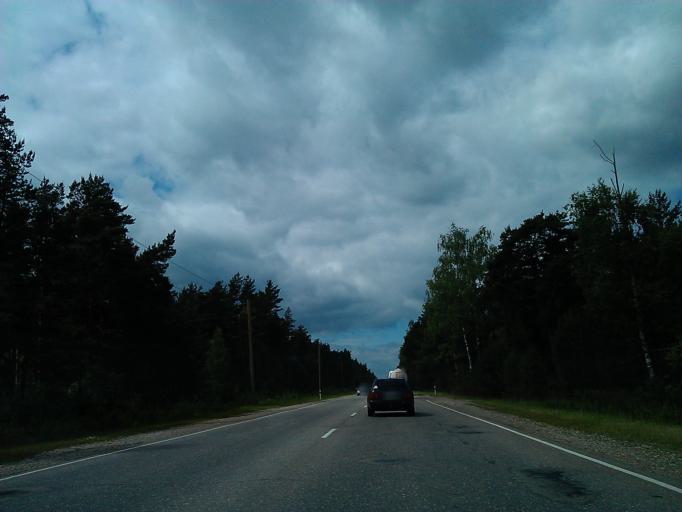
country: LV
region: Babite
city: Pinki
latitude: 56.9627
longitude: 23.8561
